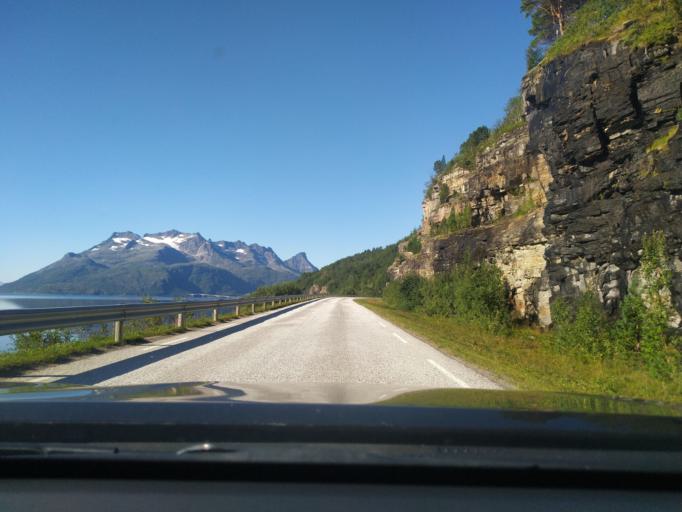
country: NO
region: Troms
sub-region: Dyroy
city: Brostadbotn
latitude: 68.9201
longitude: 17.6148
